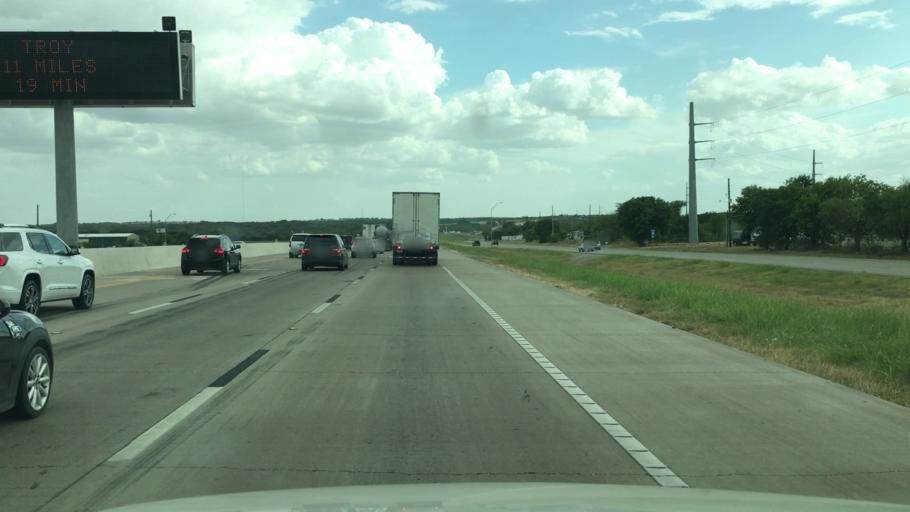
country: US
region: Texas
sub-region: McLennan County
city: Lorena
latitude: 31.3473
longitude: -97.2207
